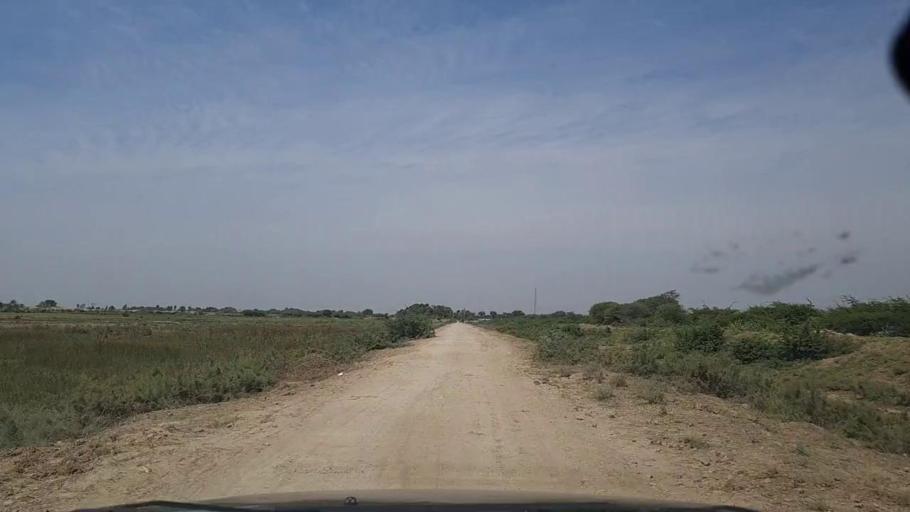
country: PK
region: Sindh
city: Mirpur Batoro
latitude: 24.6502
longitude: 68.1837
